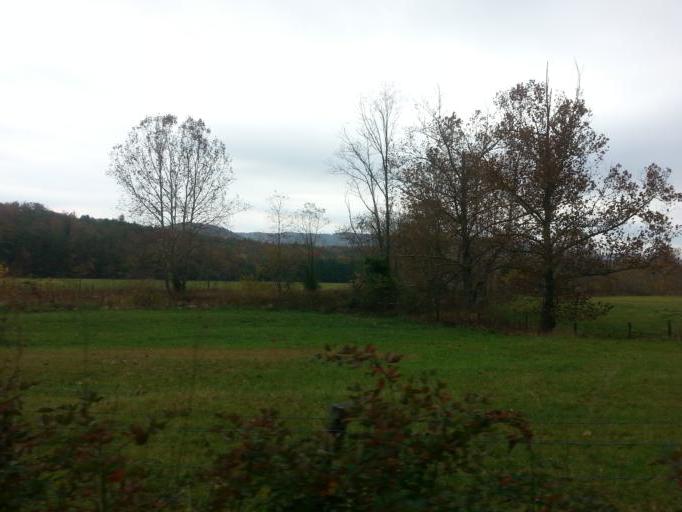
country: US
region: Virginia
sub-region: Pulaski County
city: Pulaski
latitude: 37.1036
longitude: -80.8973
